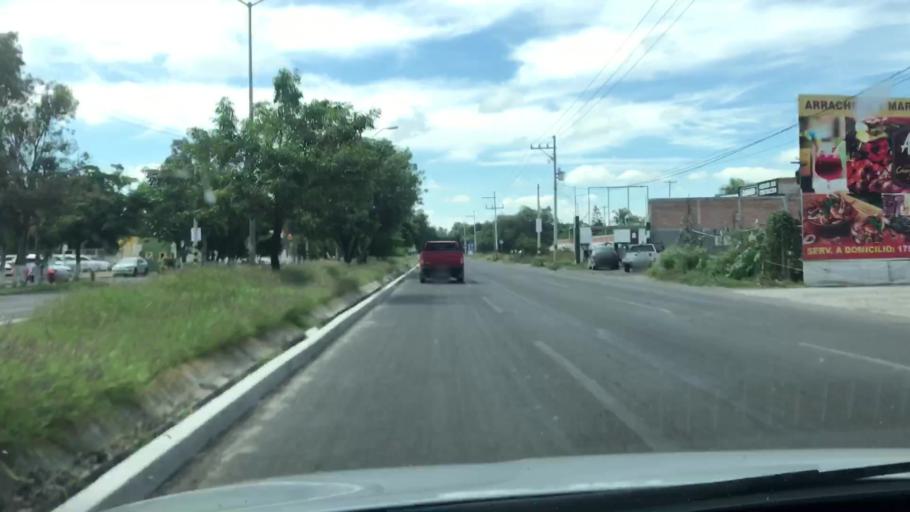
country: MX
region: Guanajuato
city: Celaya
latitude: 20.5232
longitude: -100.7785
